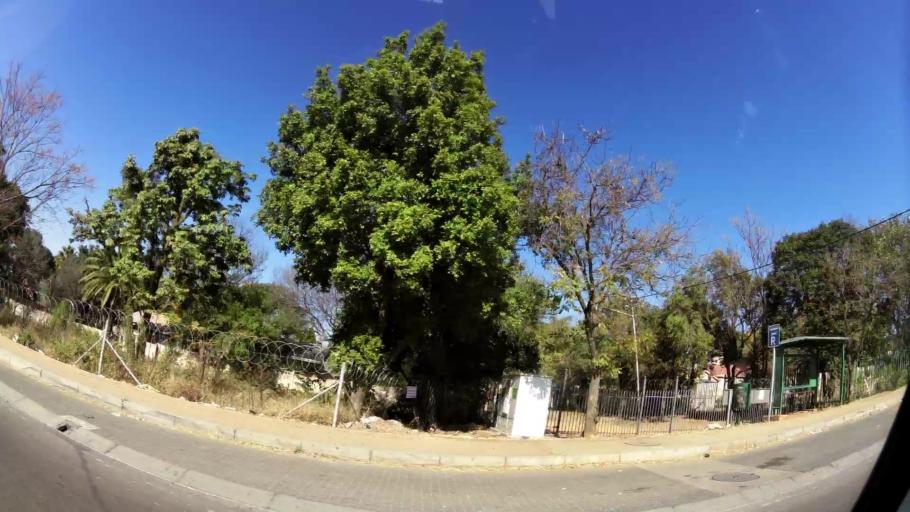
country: ZA
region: Gauteng
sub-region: City of Tshwane Metropolitan Municipality
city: Pretoria
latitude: -25.7744
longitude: 28.2660
